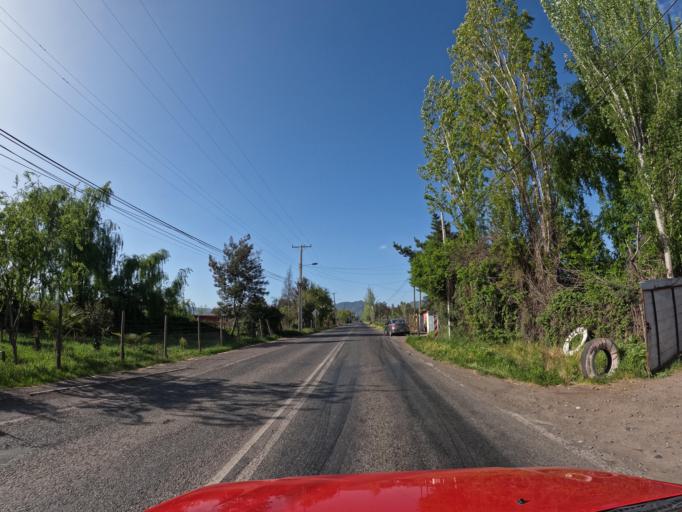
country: CL
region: Maule
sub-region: Provincia de Curico
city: Rauco
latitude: -34.8870
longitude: -71.2726
